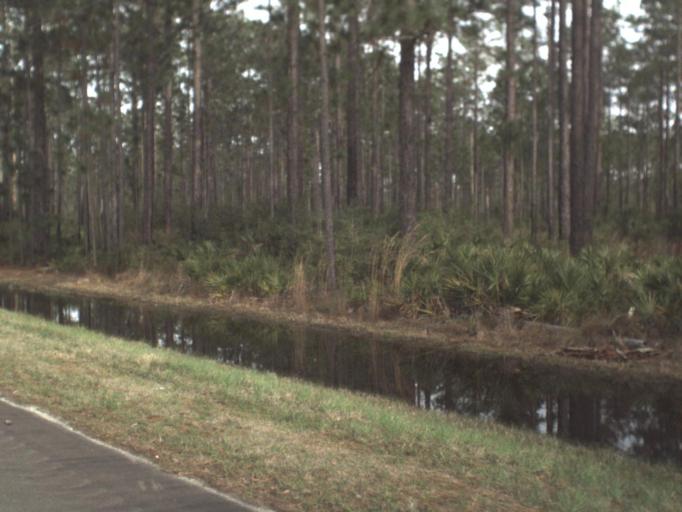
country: US
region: Florida
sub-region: Gulf County
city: Wewahitchka
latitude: 30.1399
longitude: -85.3316
